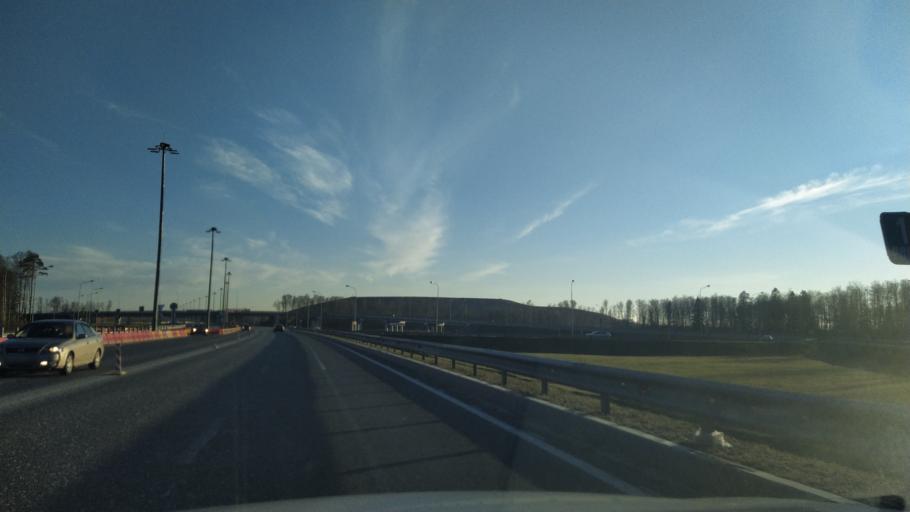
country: RU
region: St.-Petersburg
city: Levashovo
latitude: 60.0779
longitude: 30.1851
